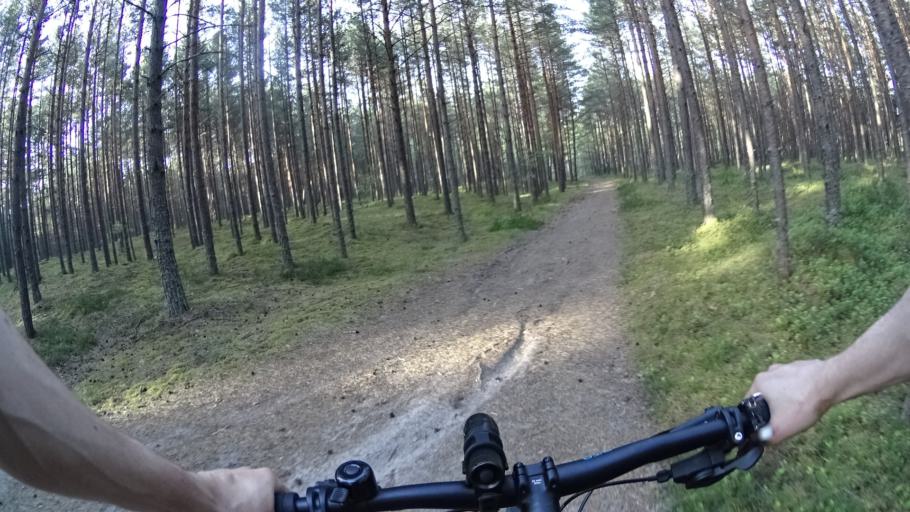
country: LV
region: Riga
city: Jaunciems
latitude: 57.0872
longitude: 24.1440
